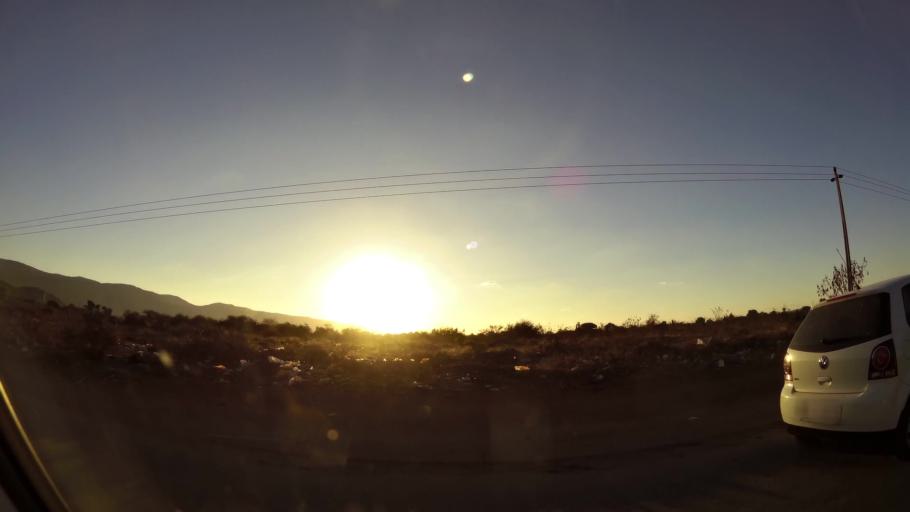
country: ZA
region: Limpopo
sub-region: Waterberg District Municipality
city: Mokopane
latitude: -24.1406
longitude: 28.9798
